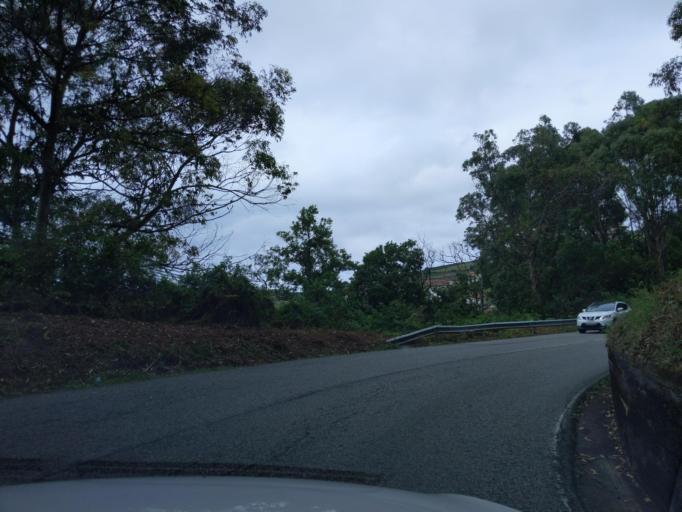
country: ES
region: Asturias
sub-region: Province of Asturias
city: Aviles
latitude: 43.5878
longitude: -5.9138
